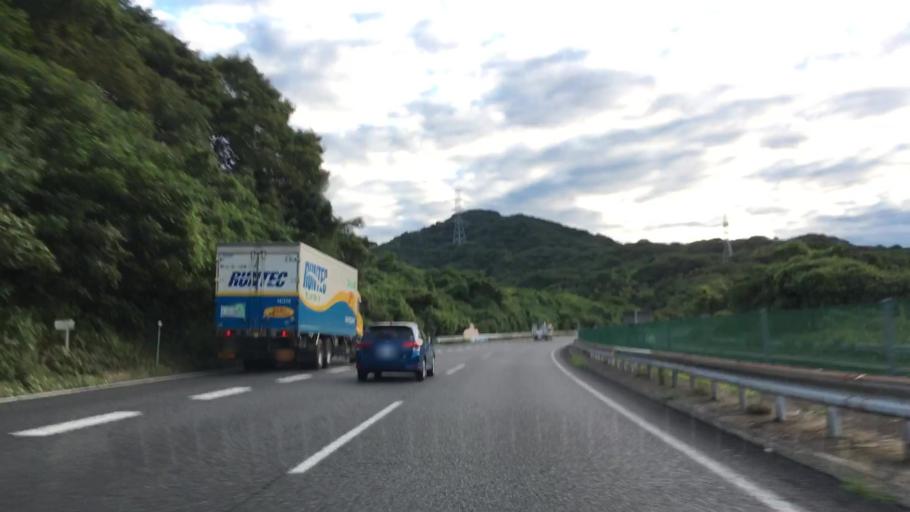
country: JP
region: Yamaguchi
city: Shimonoseki
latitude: 34.0409
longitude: 130.9843
